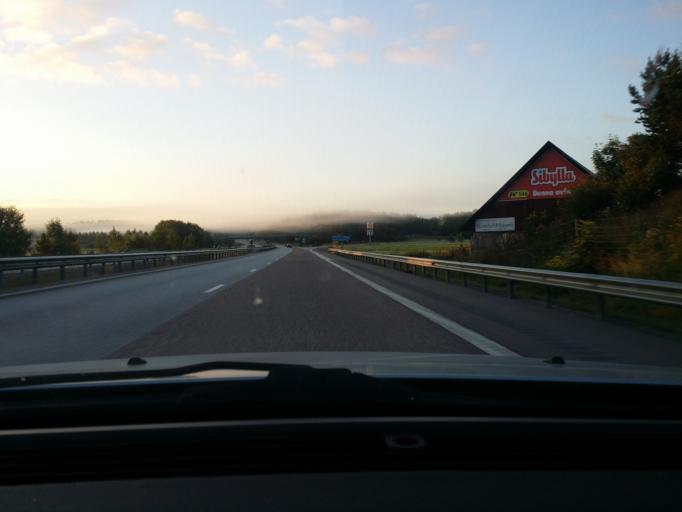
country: SE
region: Uppsala
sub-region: Habo Kommun
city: Balsta
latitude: 59.5888
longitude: 17.5005
